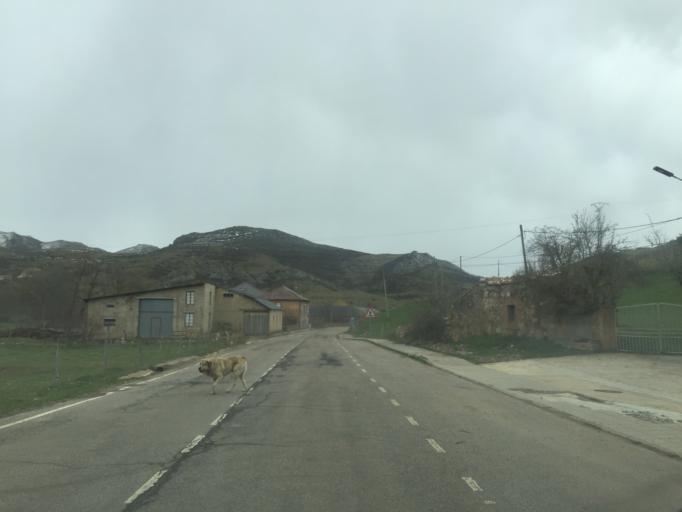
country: ES
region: Castille and Leon
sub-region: Provincia de Leon
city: San Emiliano
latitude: 43.0097
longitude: -5.9970
